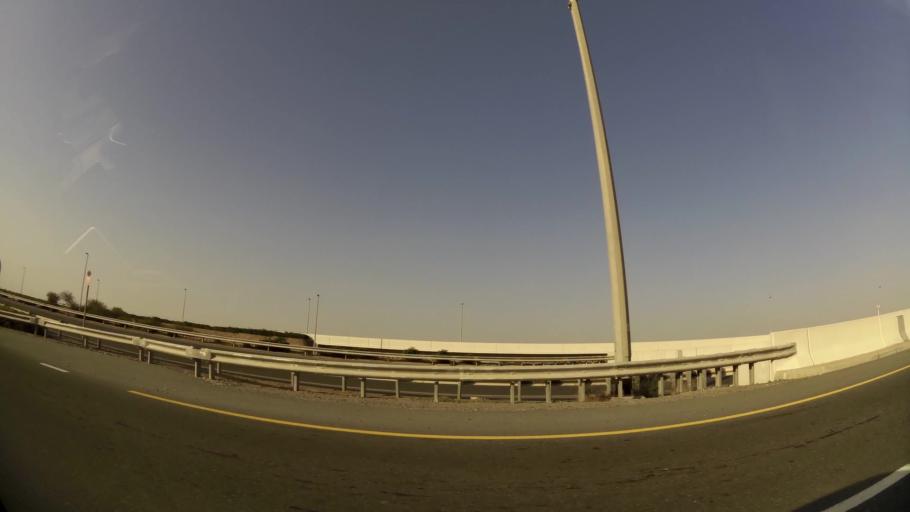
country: AE
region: Dubai
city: Dubai
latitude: 25.0572
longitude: 55.2516
